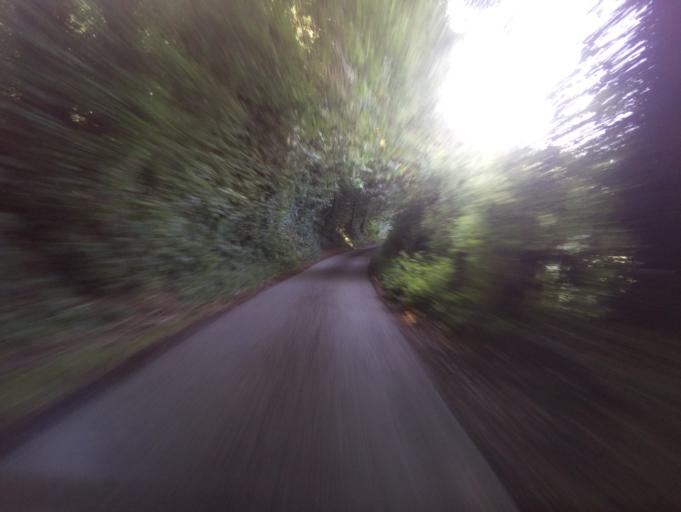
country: GB
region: England
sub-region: Herefordshire
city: Brockhampton
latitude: 51.9683
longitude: -2.5610
